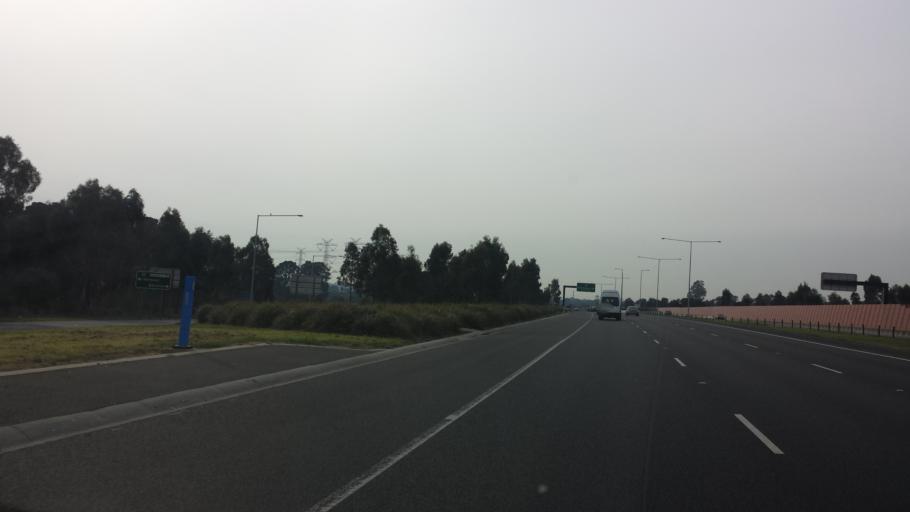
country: AU
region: Victoria
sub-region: Knox
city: Wantirna
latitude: -37.8490
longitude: 145.2162
